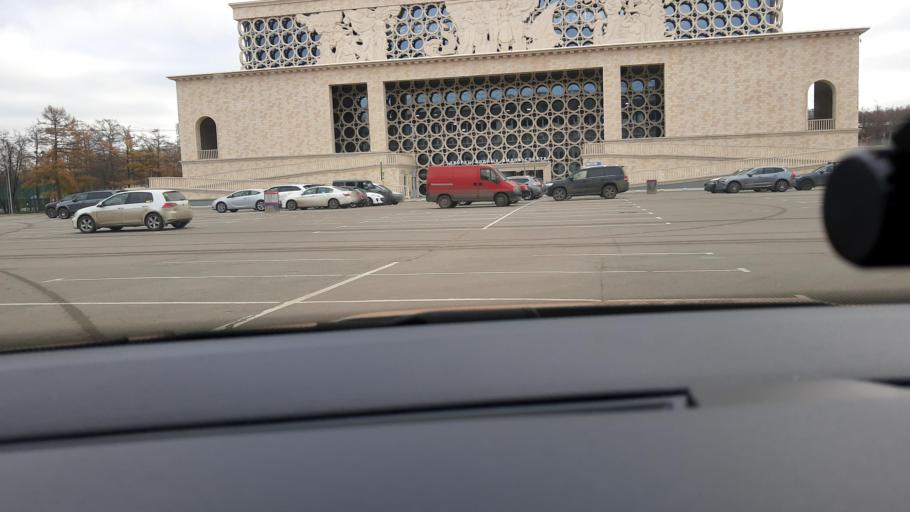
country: RU
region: Moscow
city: Luzhniki
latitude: 55.7141
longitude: 37.5562
